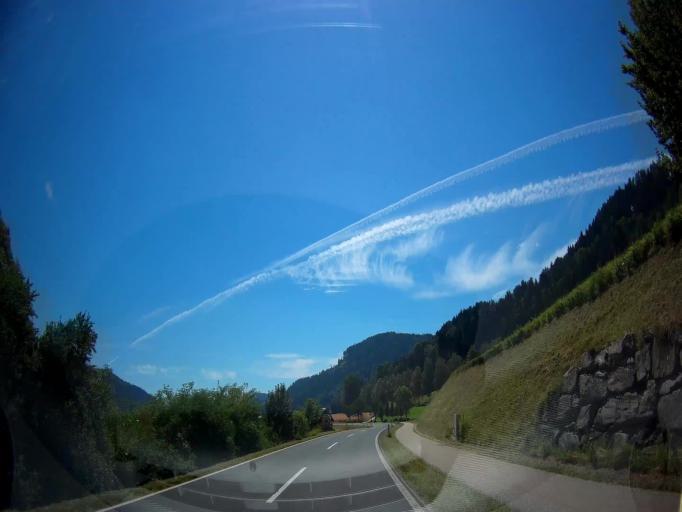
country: AT
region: Carinthia
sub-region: Politischer Bezirk Sankt Veit an der Glan
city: Micheldorf
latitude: 46.9264
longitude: 14.4277
